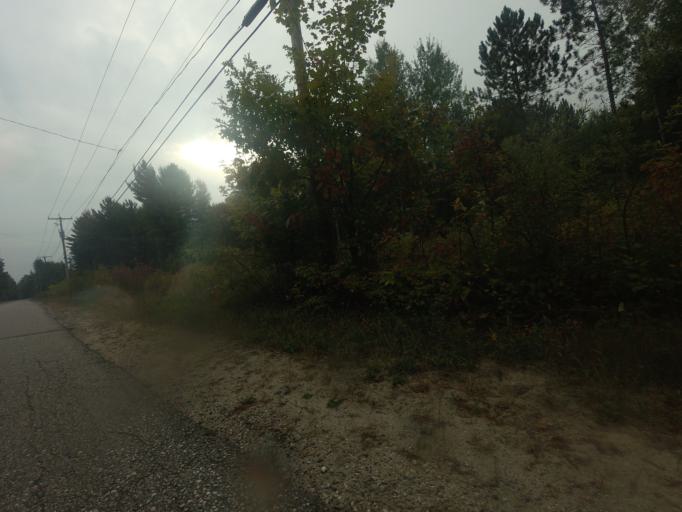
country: CA
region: Quebec
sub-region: Outaouais
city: Maniwaki
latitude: 46.0850
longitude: -76.0168
